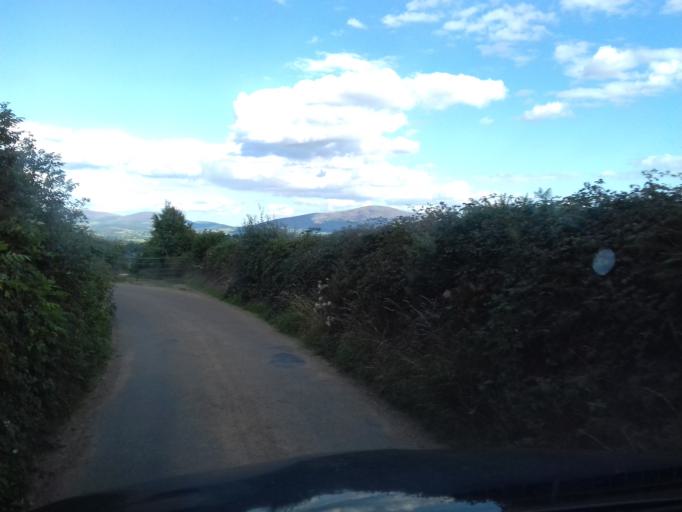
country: IE
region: Leinster
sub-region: Kilkenny
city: Graiguenamanagh
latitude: 52.5824
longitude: -7.0036
